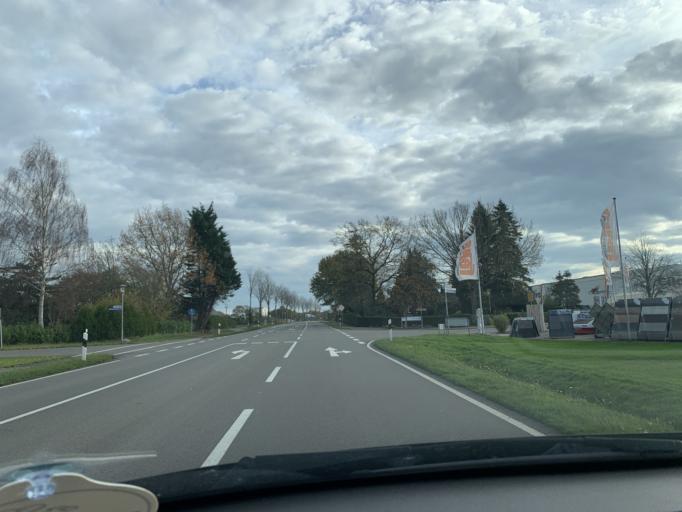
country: DE
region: Lower Saxony
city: Apen
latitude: 53.2161
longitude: 7.8020
